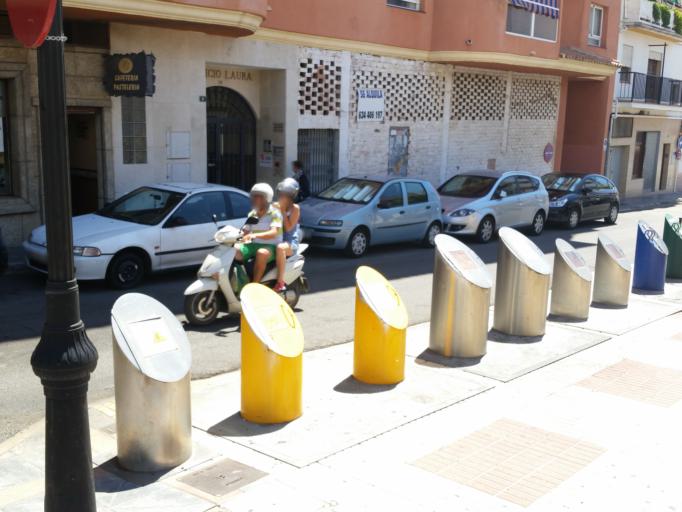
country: ES
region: Andalusia
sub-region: Provincia de Malaga
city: Fuengirola
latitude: 36.5378
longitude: -4.6267
